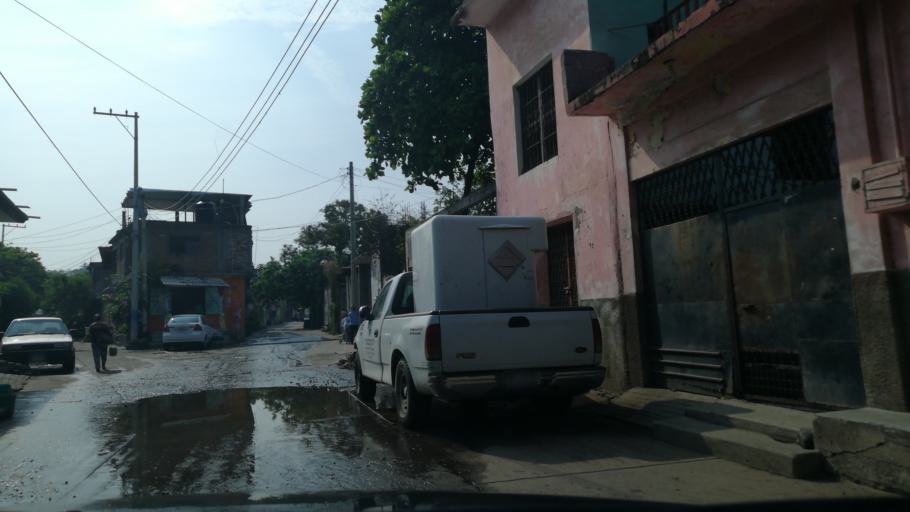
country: MX
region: Oaxaca
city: San Blas Atempa
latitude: 16.3367
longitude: -95.2292
